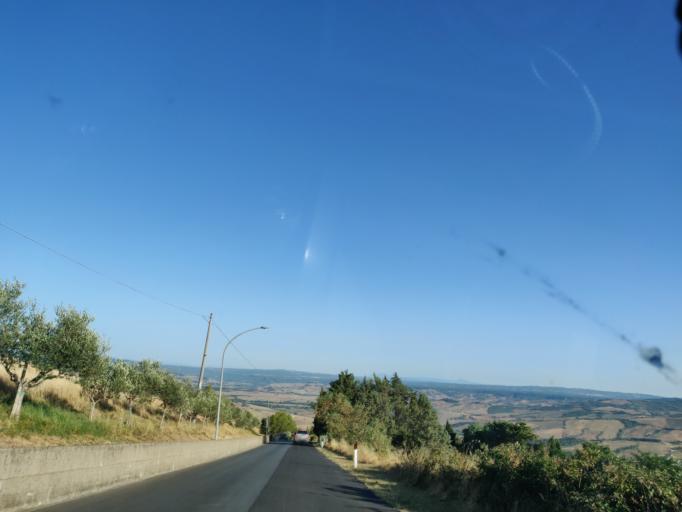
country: IT
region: Tuscany
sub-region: Provincia di Siena
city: Piancastagnaio
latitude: 42.8468
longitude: 11.6962
